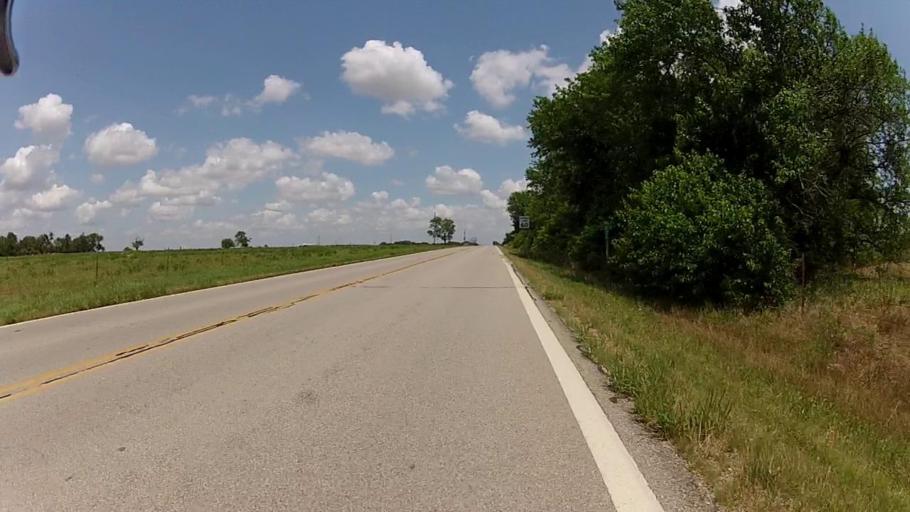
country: US
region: Kansas
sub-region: Labette County
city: Altamont
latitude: 37.1925
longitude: -95.3559
